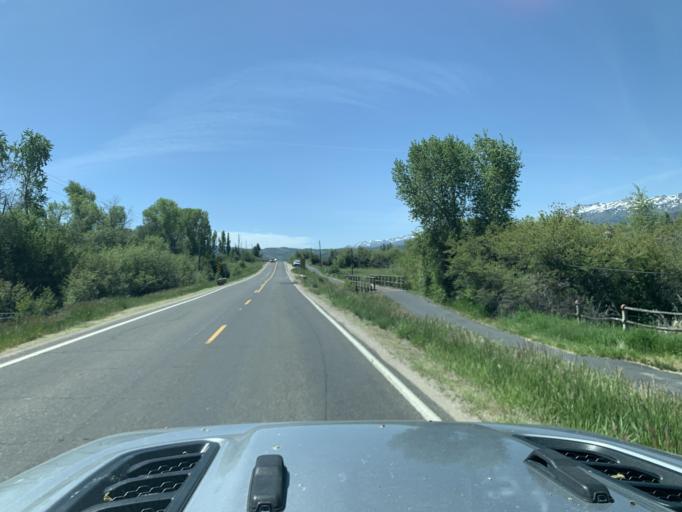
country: US
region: Utah
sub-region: Weber County
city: Wolf Creek
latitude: 41.2883
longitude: -111.7770
